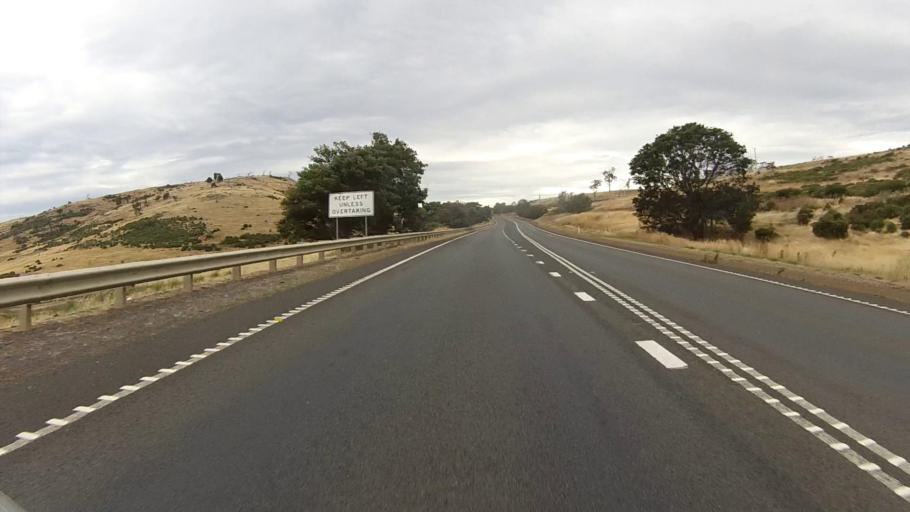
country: AU
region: Tasmania
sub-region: Brighton
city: Bridgewater
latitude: -42.3417
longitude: 147.3398
